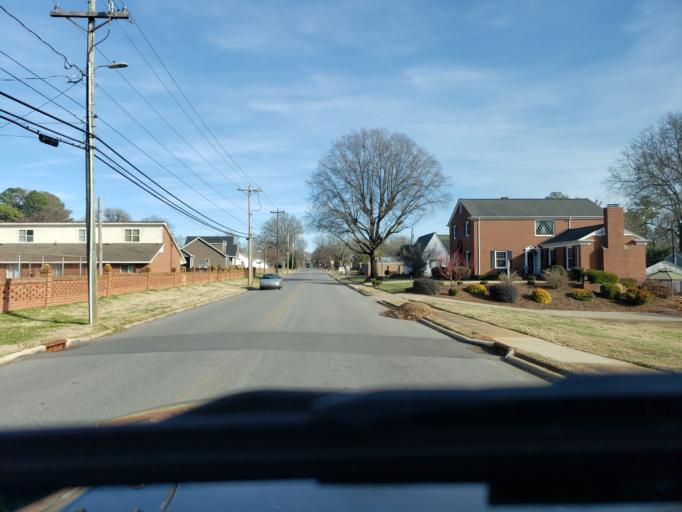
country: US
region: North Carolina
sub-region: Cleveland County
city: Kings Mountain
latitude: 35.2394
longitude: -81.3579
